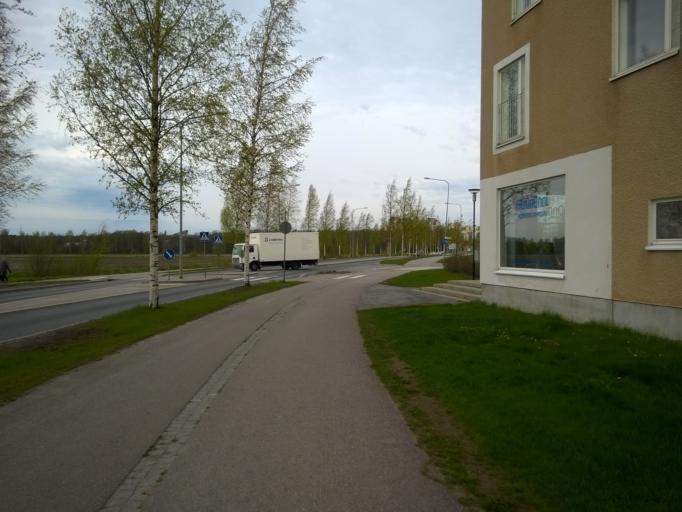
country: FI
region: Uusimaa
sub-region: Helsinki
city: Vantaa
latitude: 60.2244
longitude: 25.0131
